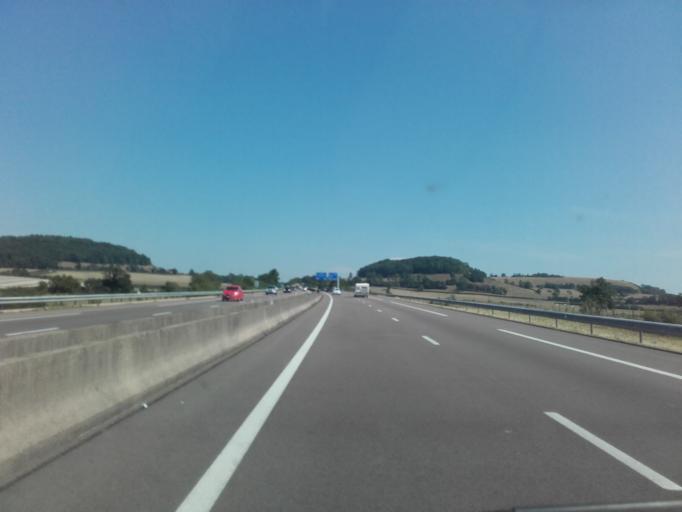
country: FR
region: Bourgogne
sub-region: Departement de la Cote-d'Or
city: Pouilly-en-Auxois
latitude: 47.2571
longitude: 4.5319
